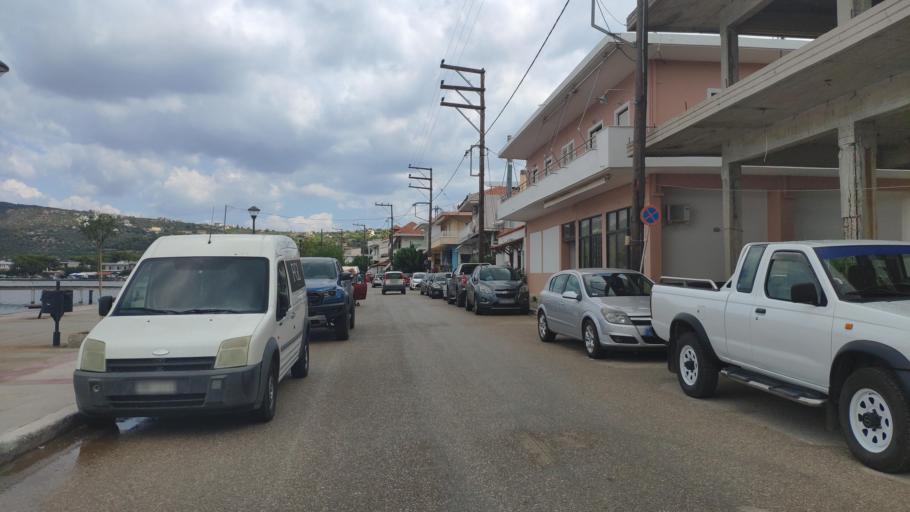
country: GR
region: Central Greece
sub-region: Nomos Fthiotidos
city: Malesina
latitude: 38.6529
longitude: 23.1922
